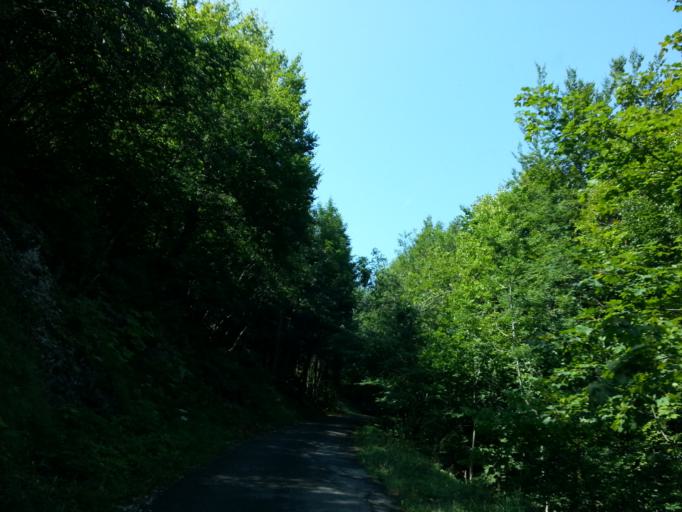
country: FR
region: Rhone-Alpes
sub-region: Departement de la Haute-Savoie
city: Veyrier-du-Lac
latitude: 45.9091
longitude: 6.1761
